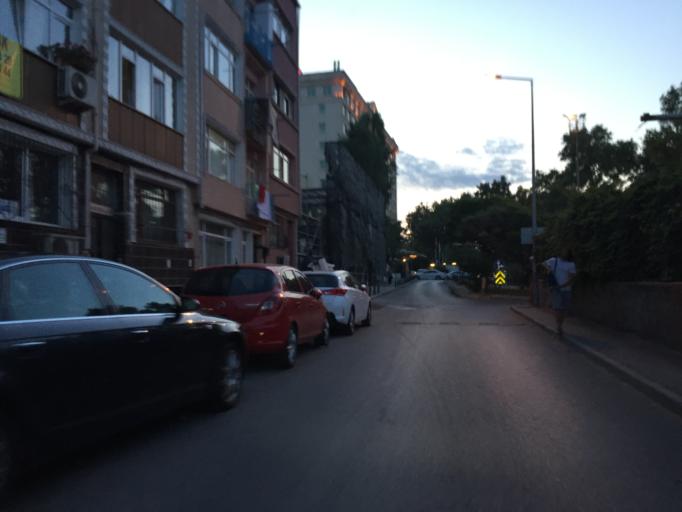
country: TR
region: Istanbul
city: Istanbul
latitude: 41.0222
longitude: 28.9315
